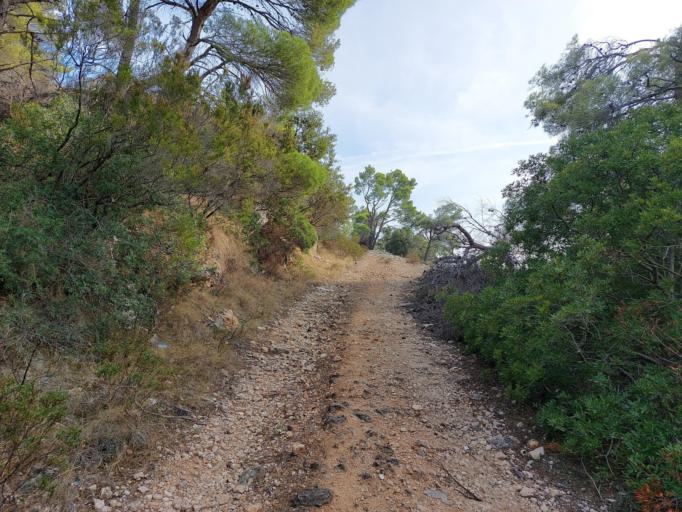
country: HR
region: Dubrovacko-Neretvanska
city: Smokvica
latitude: 42.7340
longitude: 16.8295
